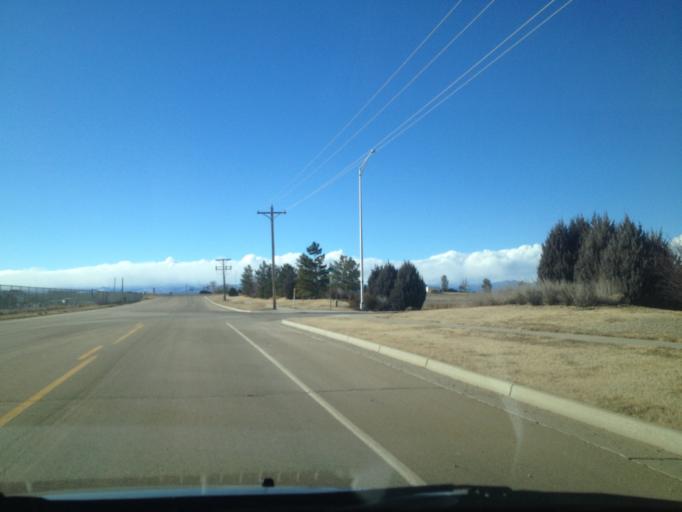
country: US
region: Colorado
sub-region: Weld County
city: Dacono
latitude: 40.0731
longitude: -104.9774
